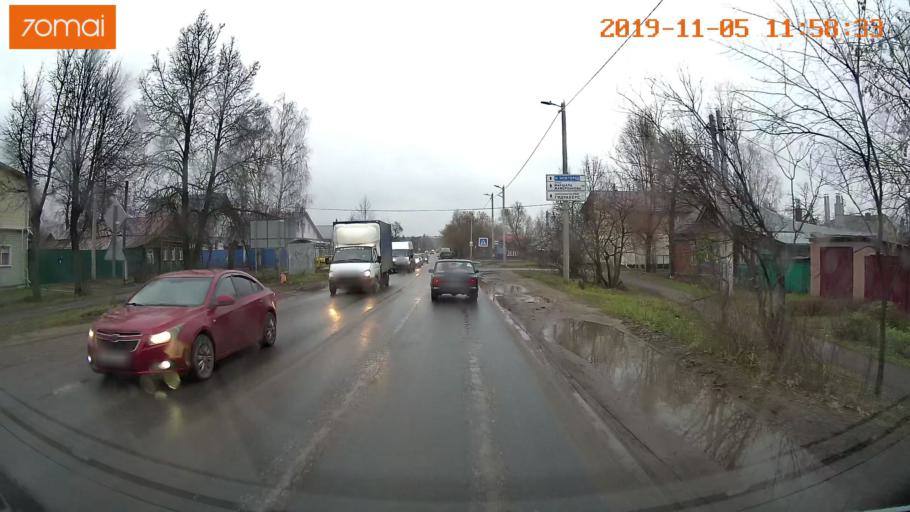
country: RU
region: Ivanovo
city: Kokhma
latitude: 56.9809
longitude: 41.0404
